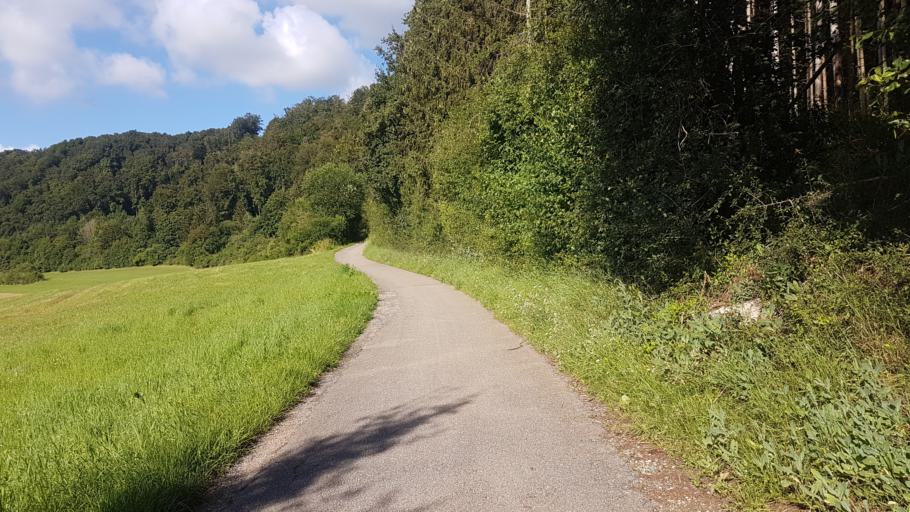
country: DE
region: Bavaria
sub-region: Upper Bavaria
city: Walting
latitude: 48.9474
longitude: 11.3552
